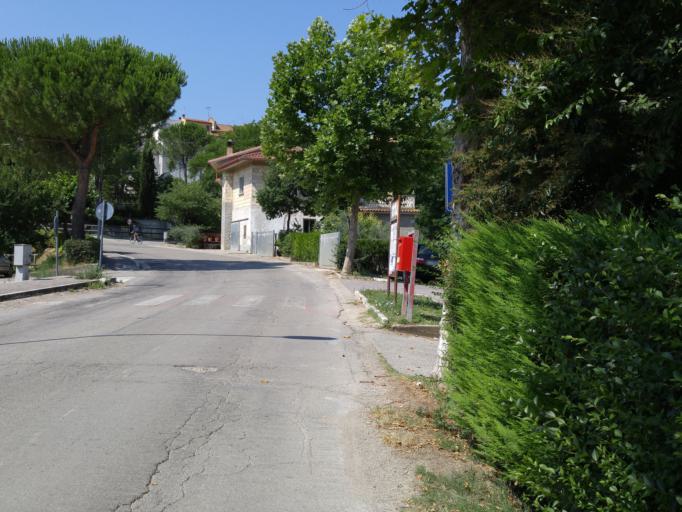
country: IT
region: Abruzzo
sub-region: Provincia di Teramo
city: Castilenti
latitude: 42.5342
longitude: 13.9191
